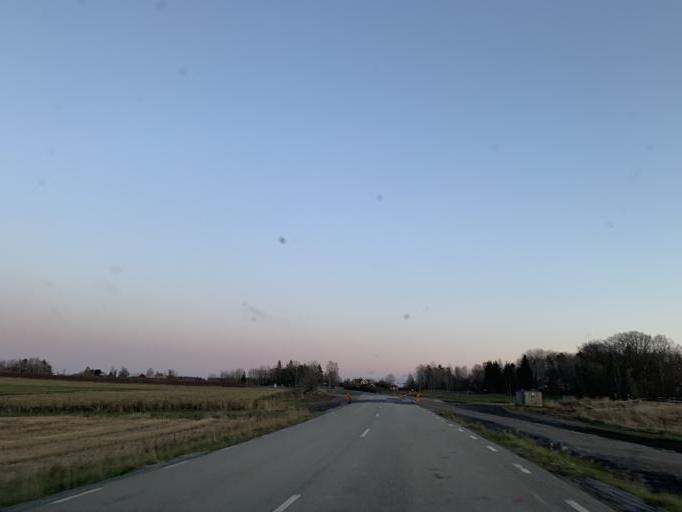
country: SE
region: OErebro
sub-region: Orebro Kommun
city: Hovsta
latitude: 59.3111
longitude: 15.3535
